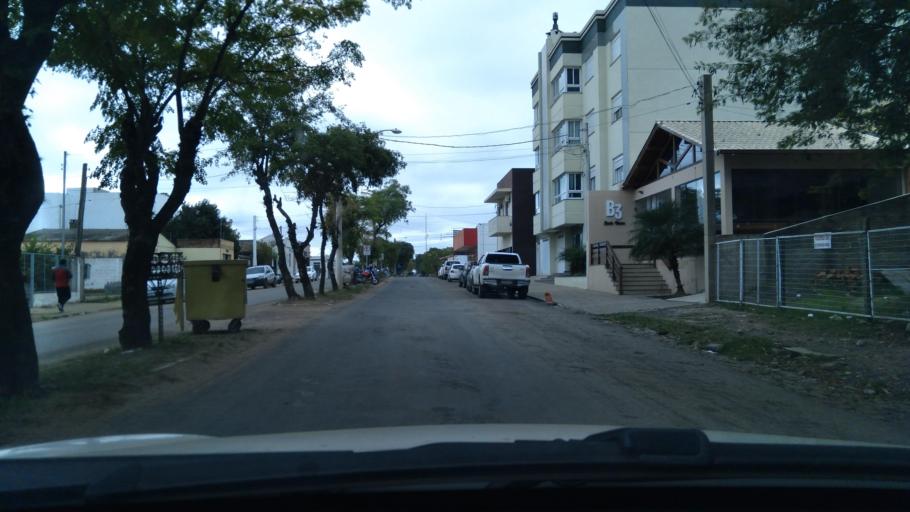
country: BR
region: Rio Grande do Sul
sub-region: Dom Pedrito
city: Dom Pedrito
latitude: -30.9730
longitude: -54.6738
